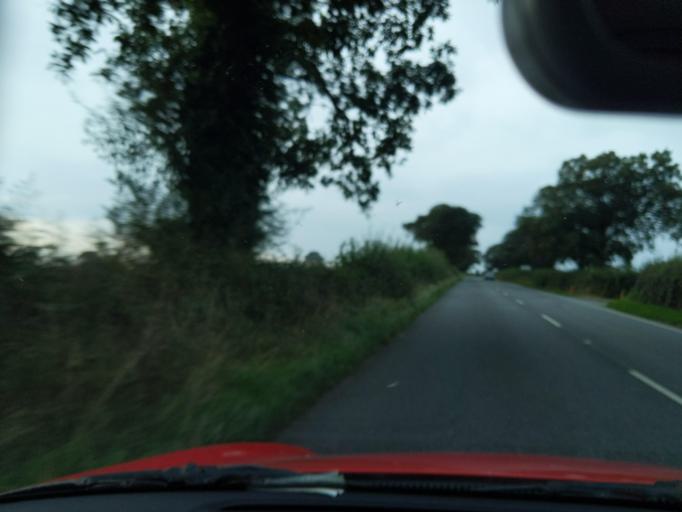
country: GB
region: England
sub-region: Devon
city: Okehampton
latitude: 50.7886
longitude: -4.0349
